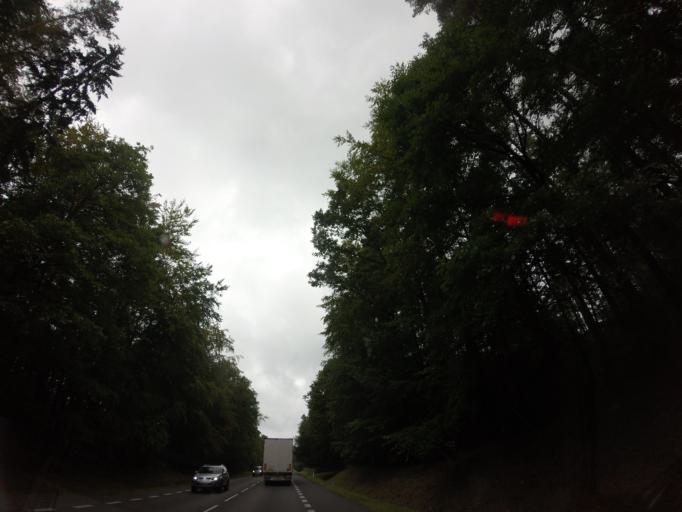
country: PL
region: West Pomeranian Voivodeship
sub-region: Powiat kamienski
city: Miedzyzdroje
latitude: 53.8865
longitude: 14.5030
